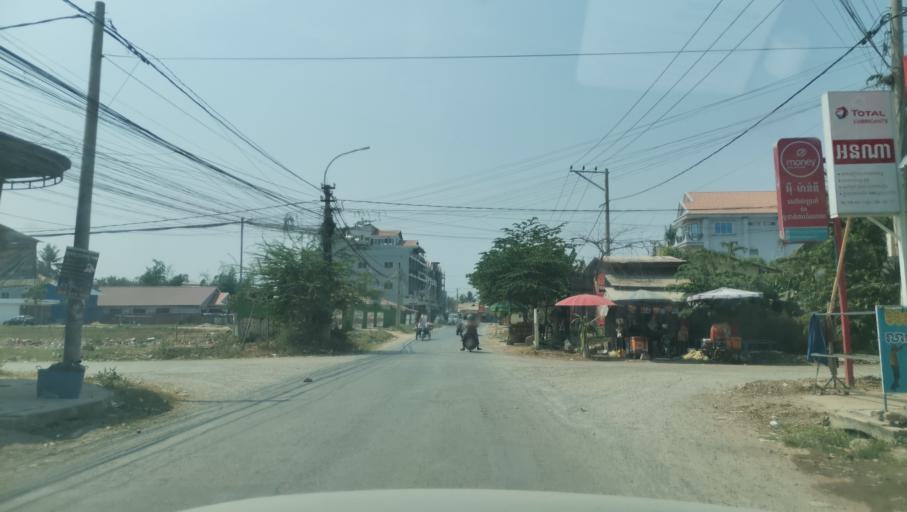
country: KH
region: Battambang
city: Battambang
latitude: 13.0905
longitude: 103.1954
